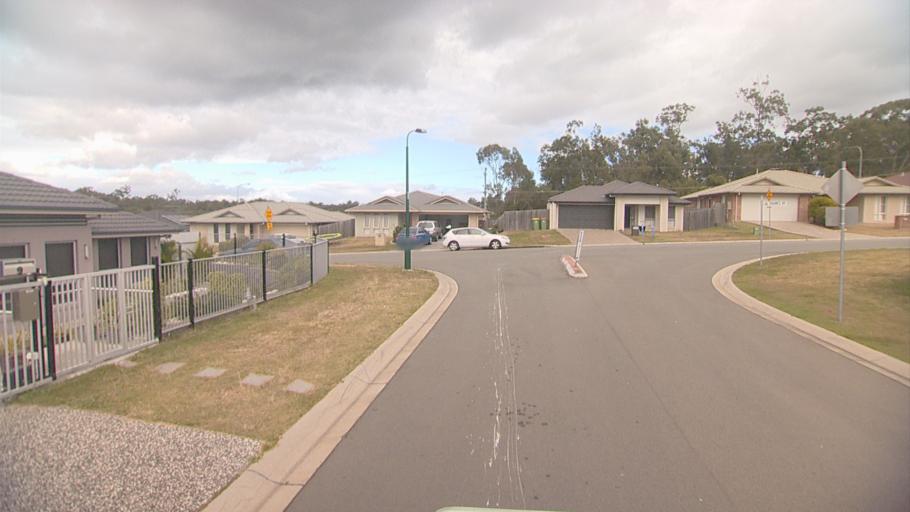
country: AU
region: Queensland
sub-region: Logan
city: Park Ridge South
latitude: -27.6882
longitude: 153.0476
